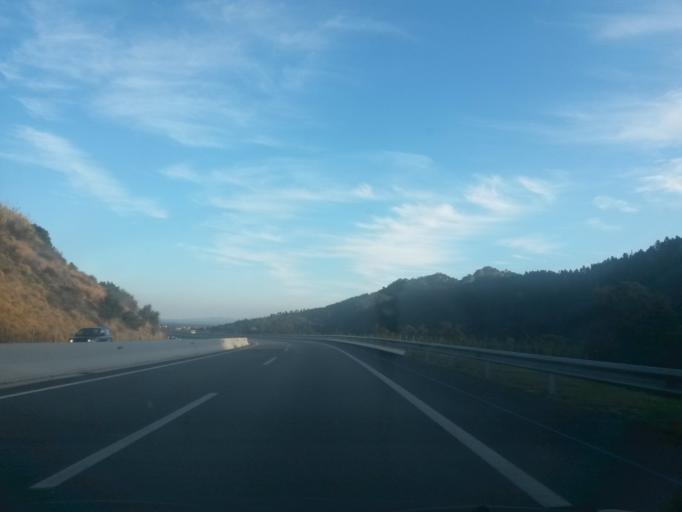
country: ES
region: Catalonia
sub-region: Provincia de Girona
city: Santa Coloma de Farners
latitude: 41.8738
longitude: 2.6150
